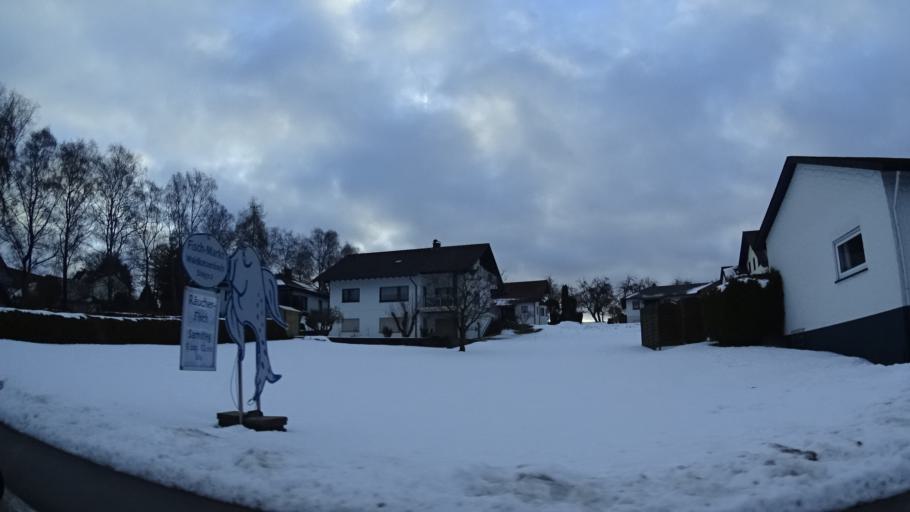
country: DE
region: Baden-Wuerttemberg
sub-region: Karlsruhe Region
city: Zwingenberg
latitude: 49.4514
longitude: 9.0592
